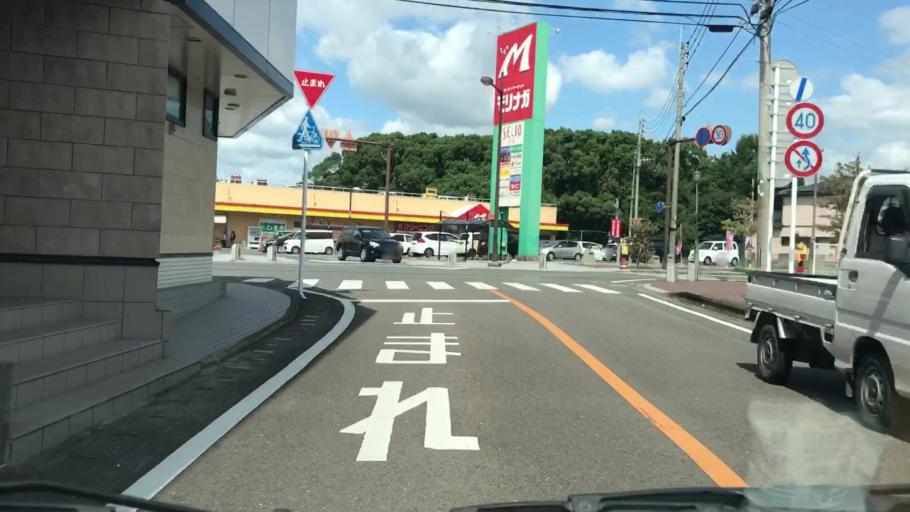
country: JP
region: Saga Prefecture
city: Saga-shi
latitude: 33.2479
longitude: 130.2043
